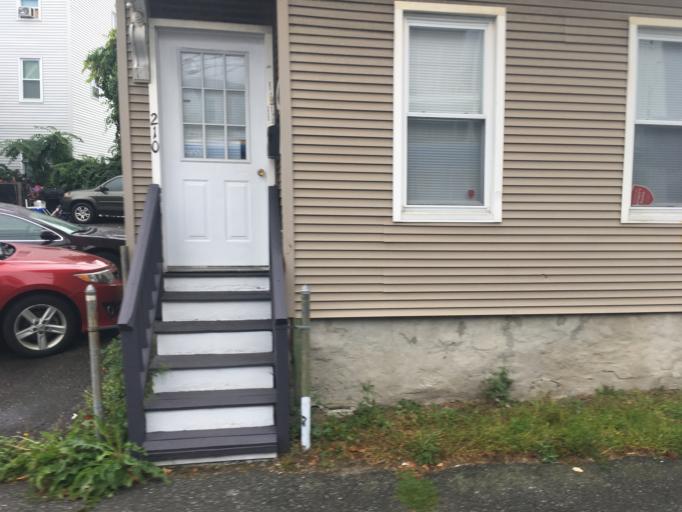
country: US
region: Massachusetts
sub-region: Middlesex County
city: Lowell
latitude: 42.6492
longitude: -71.3230
